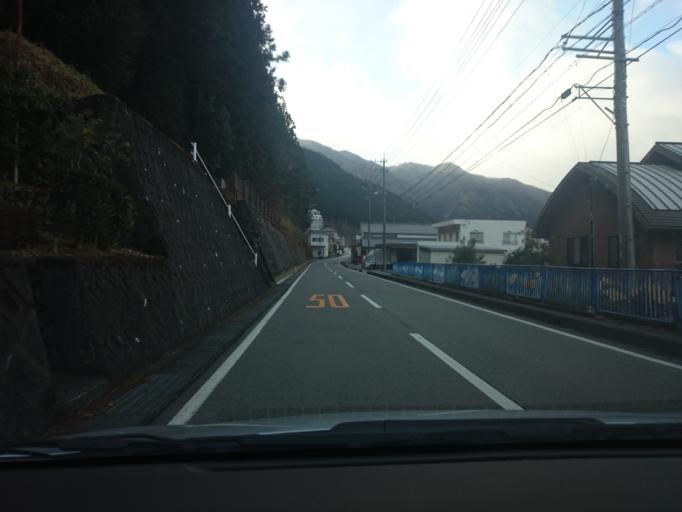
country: JP
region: Gifu
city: Gujo
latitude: 35.7977
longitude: 137.2503
